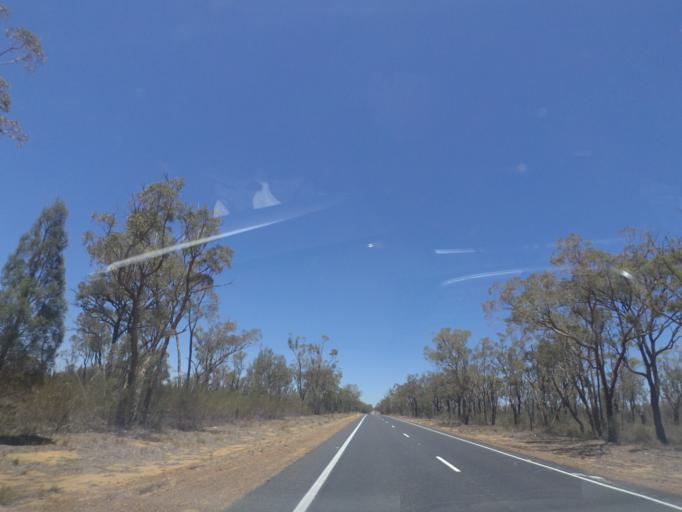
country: AU
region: New South Wales
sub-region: Narrabri
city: Narrabri
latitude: -30.7444
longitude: 149.5138
